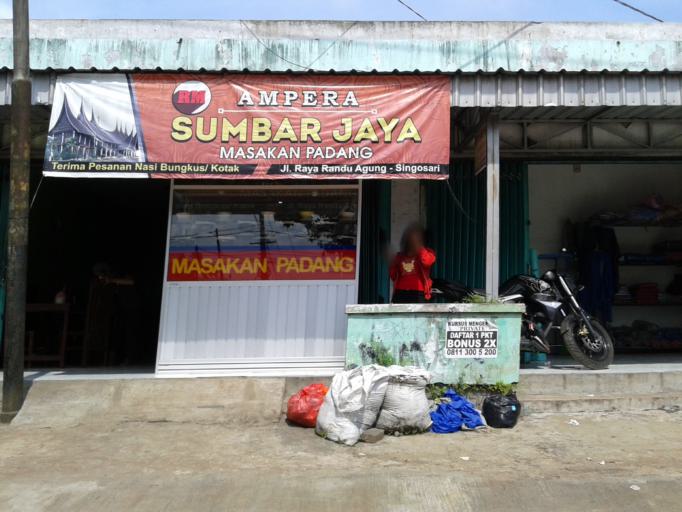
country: ID
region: East Java
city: Singosari
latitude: -7.8693
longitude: 112.6801
